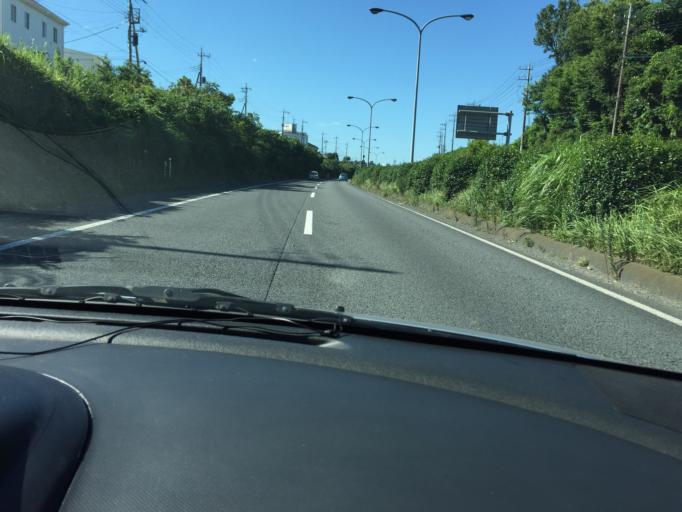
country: JP
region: Ibaraki
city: Naka
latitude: 36.0730
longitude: 140.1792
